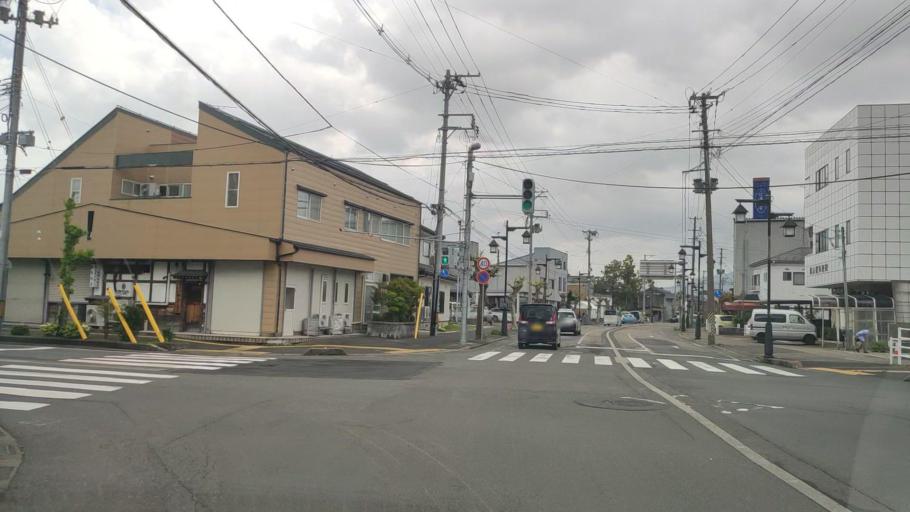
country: JP
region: Niigata
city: Gosen
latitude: 37.7380
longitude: 139.1803
